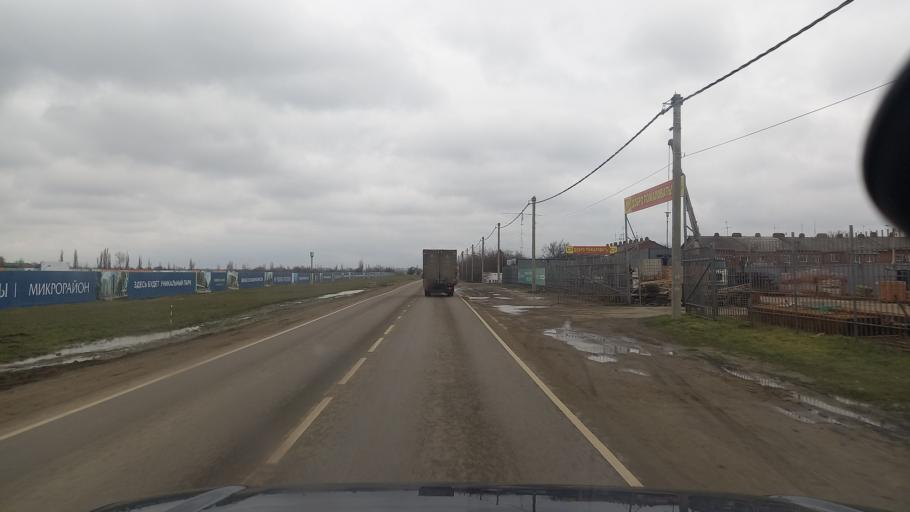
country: RU
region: Krasnodarskiy
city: Pashkovskiy
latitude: 45.0590
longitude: 39.1431
